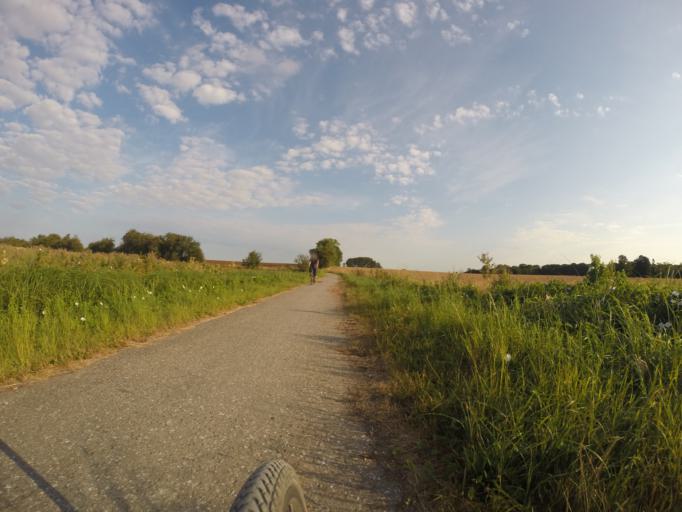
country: DK
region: Capital Region
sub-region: Egedal Kommune
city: Smorumnedre
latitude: 55.6955
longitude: 12.3151
